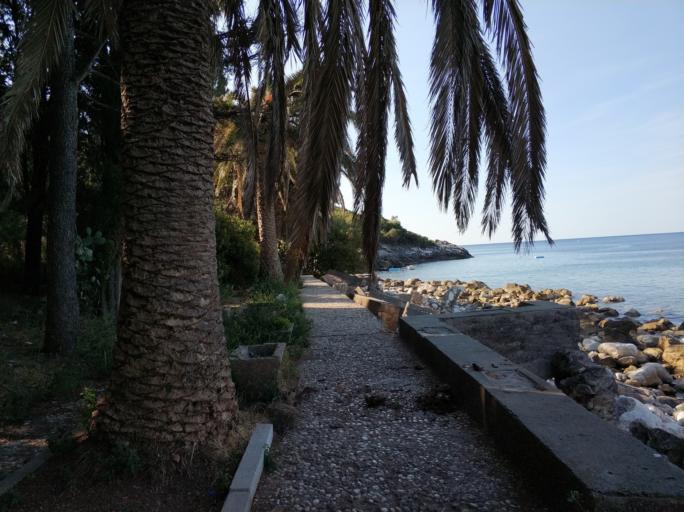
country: ME
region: Budva
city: Budva
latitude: 42.2728
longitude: 18.8884
